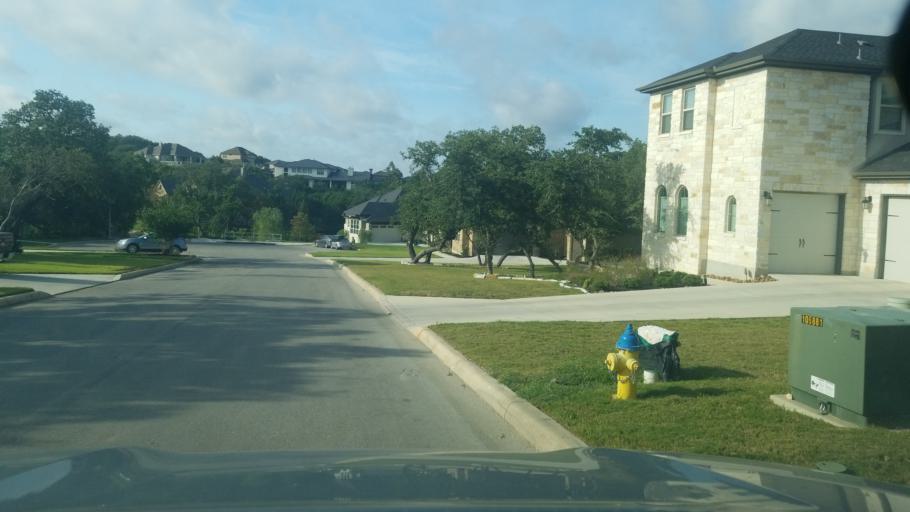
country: US
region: Texas
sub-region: Bexar County
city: Timberwood Park
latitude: 29.6882
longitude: -98.5202
